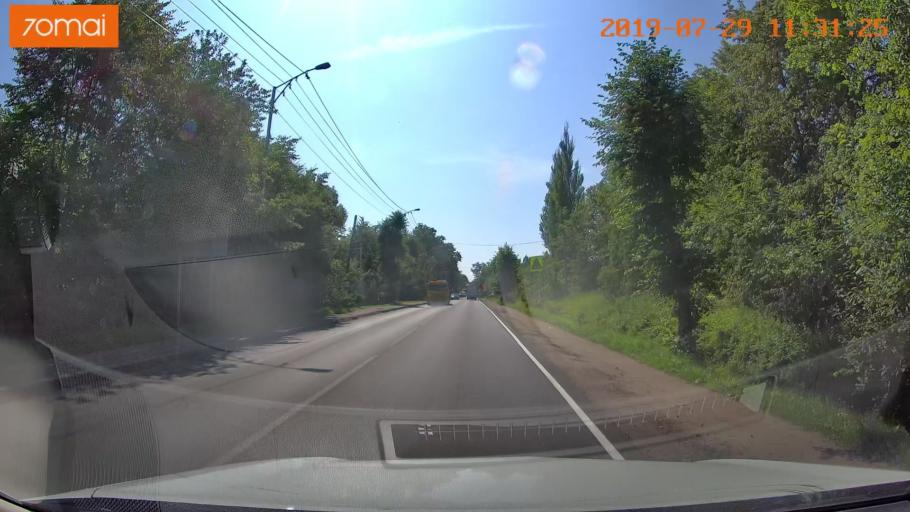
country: RU
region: Kaliningrad
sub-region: Gorod Kaliningrad
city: Kaliningrad
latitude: 54.6752
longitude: 20.5415
